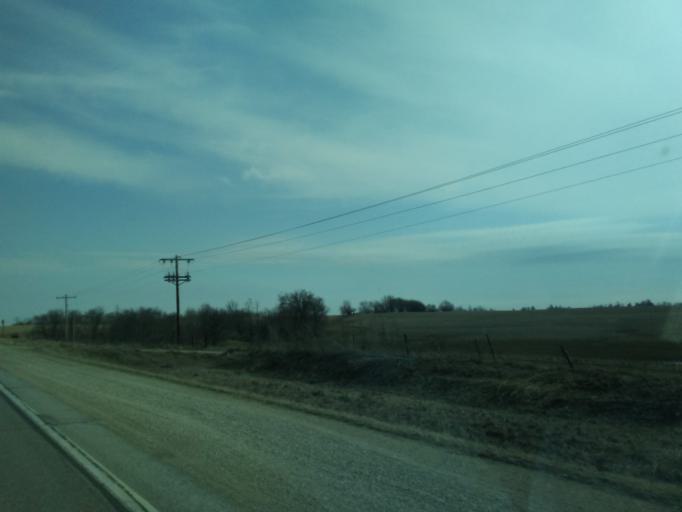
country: US
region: Iowa
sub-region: Winneshiek County
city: Decorah
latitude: 43.2433
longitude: -91.6954
